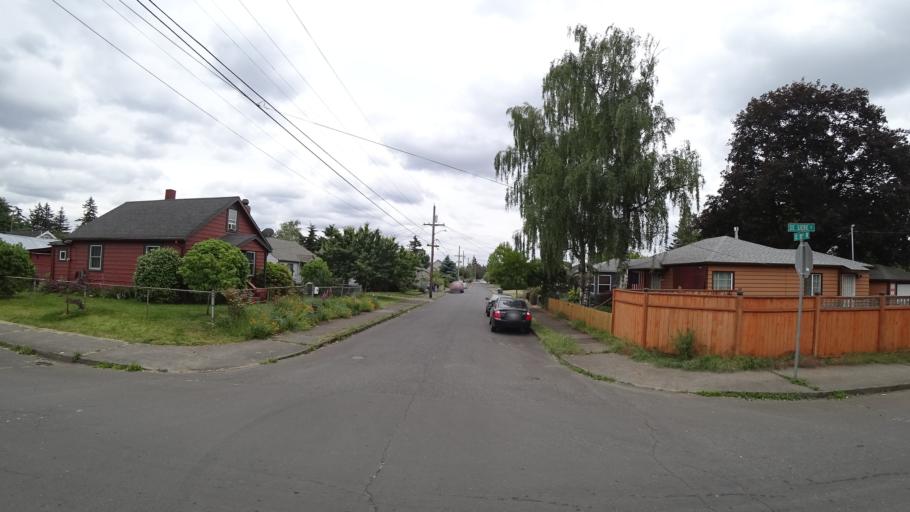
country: US
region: Oregon
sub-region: Multnomah County
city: Lents
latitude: 45.4869
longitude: -122.5759
